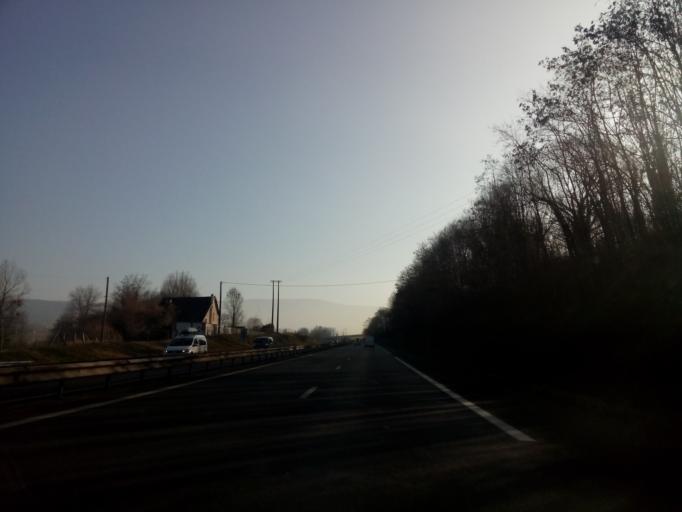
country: FR
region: Rhone-Alpes
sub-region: Departement de la Savoie
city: Le Pont-de-Beauvoisin
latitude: 45.5674
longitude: 5.6721
